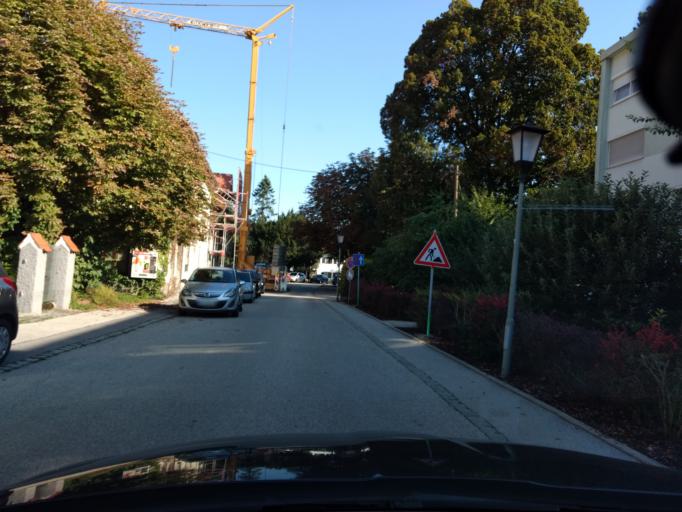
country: DE
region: Bavaria
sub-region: Upper Bavaria
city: Wolfratshausen
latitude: 47.9106
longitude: 11.4167
